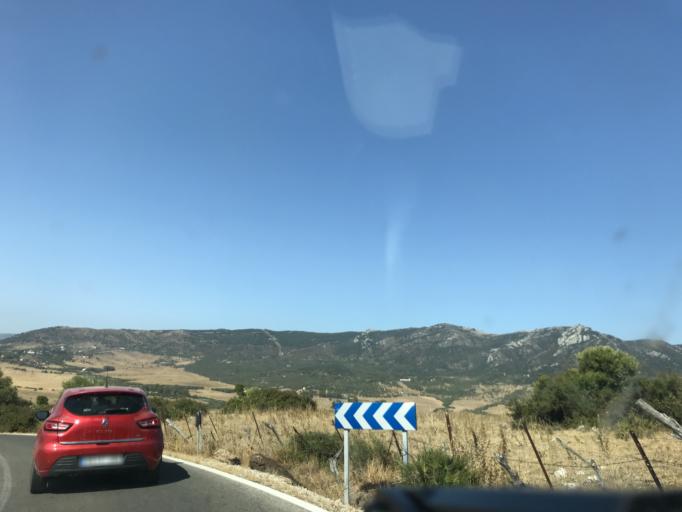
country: ES
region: Andalusia
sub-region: Provincia de Cadiz
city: Zahara de los Atunes
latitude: 36.1009
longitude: -5.7203
